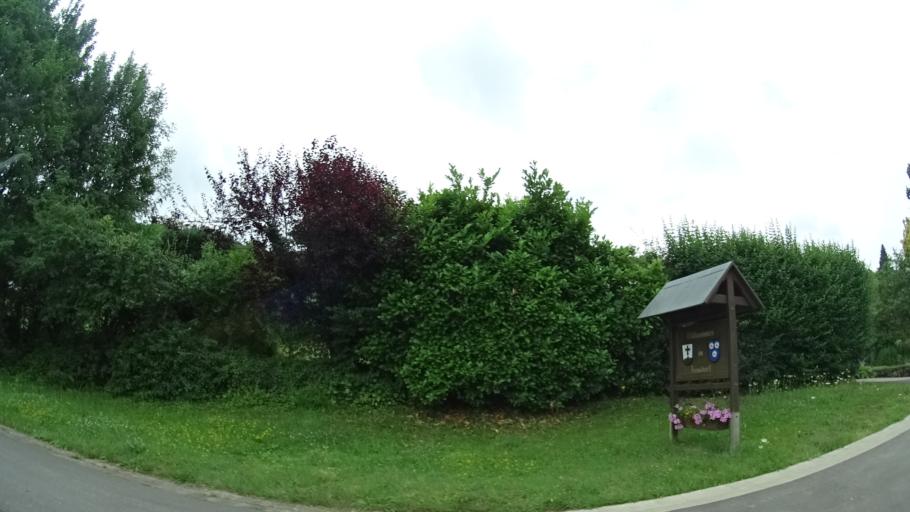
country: DE
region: Saarland
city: Orscholz
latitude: 49.4714
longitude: 6.5008
